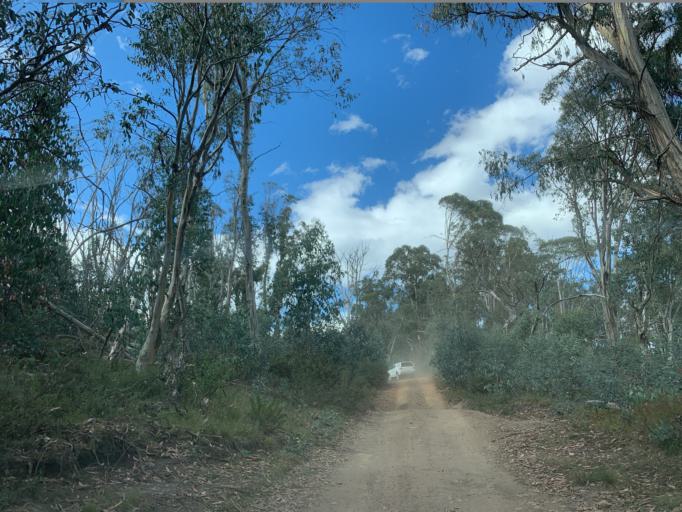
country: AU
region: Victoria
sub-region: Mansfield
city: Mansfield
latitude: -37.1020
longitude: 146.5425
